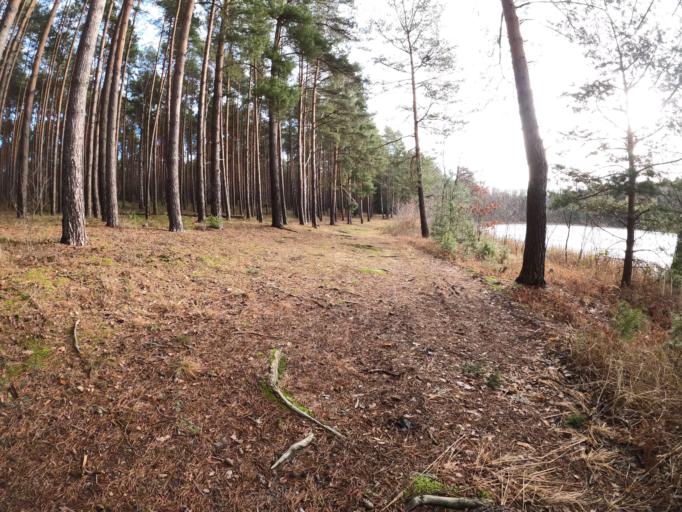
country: PL
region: Lubusz
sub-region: Powiat slubicki
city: Cybinka
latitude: 52.2477
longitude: 14.8020
